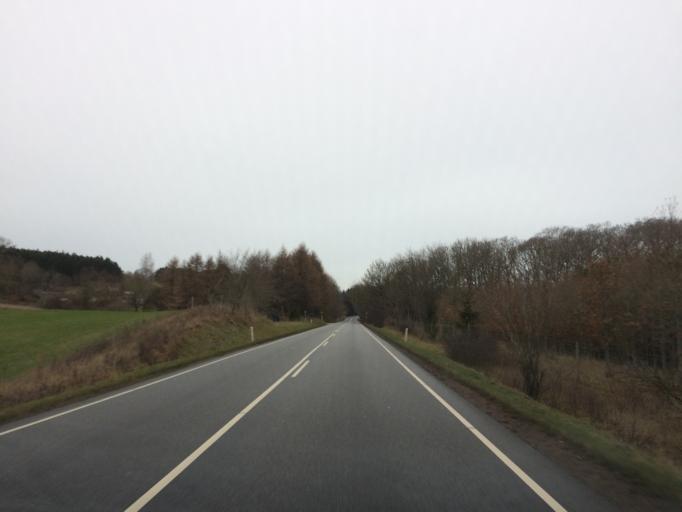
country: DK
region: Zealand
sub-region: Holbaek Kommune
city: Jyderup
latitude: 55.6261
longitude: 11.3956
